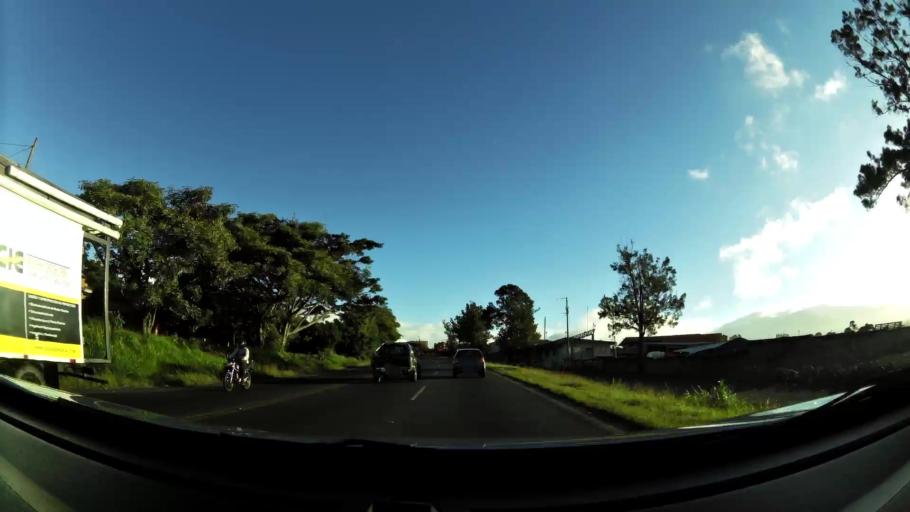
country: CR
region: Heredia
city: Angeles
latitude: 9.9808
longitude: -84.0486
